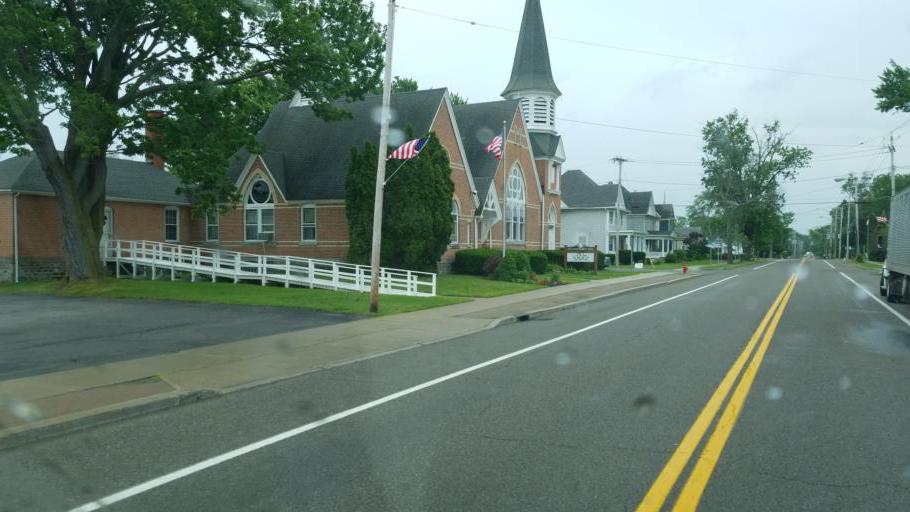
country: US
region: New York
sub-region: Niagara County
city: Wilson
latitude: 43.3090
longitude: -78.8260
